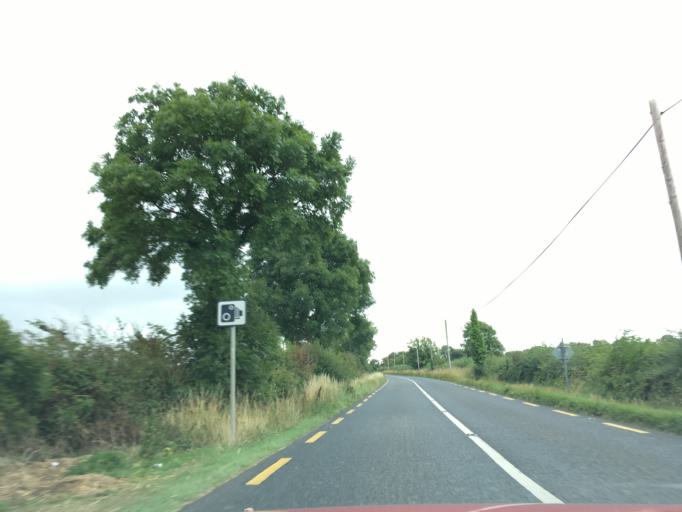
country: IE
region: Munster
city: Fethard
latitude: 52.4410
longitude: -7.7987
